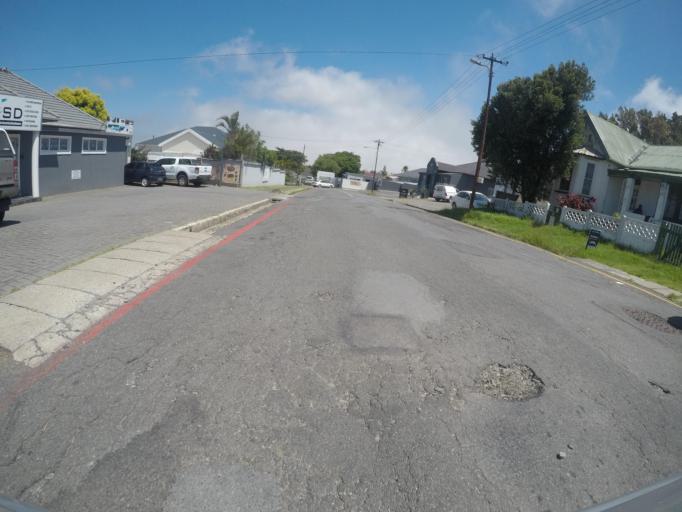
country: ZA
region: Eastern Cape
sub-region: Buffalo City Metropolitan Municipality
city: East London
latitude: -32.9854
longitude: 27.9011
